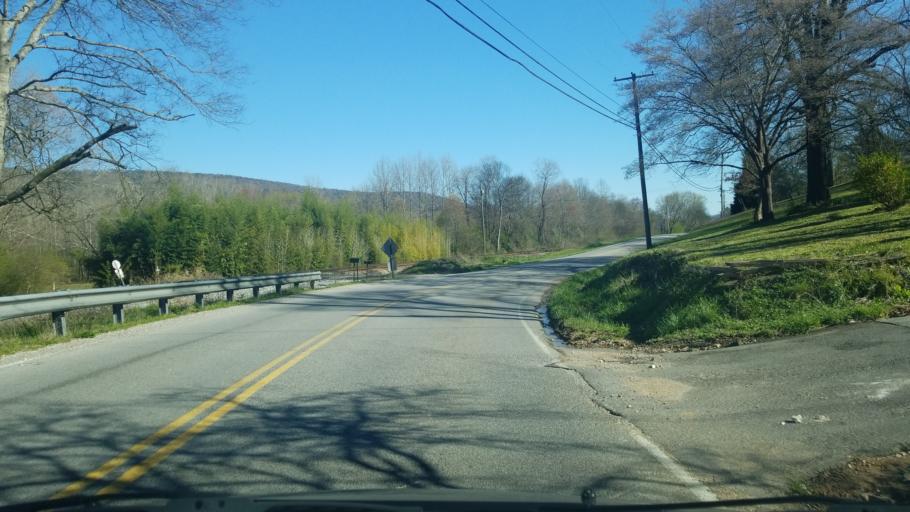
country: US
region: Tennessee
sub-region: Hamilton County
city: Soddy-Daisy
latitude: 35.2254
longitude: -85.1980
